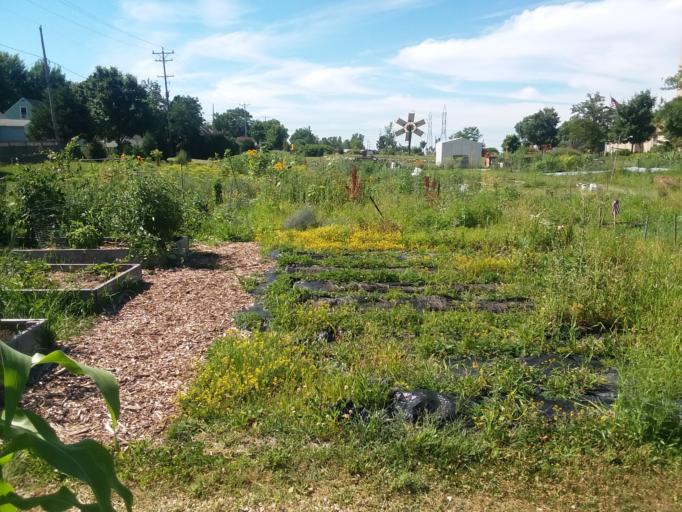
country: US
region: Wisconsin
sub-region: Milwaukee County
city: Saint Francis
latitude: 42.9734
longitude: -87.9188
